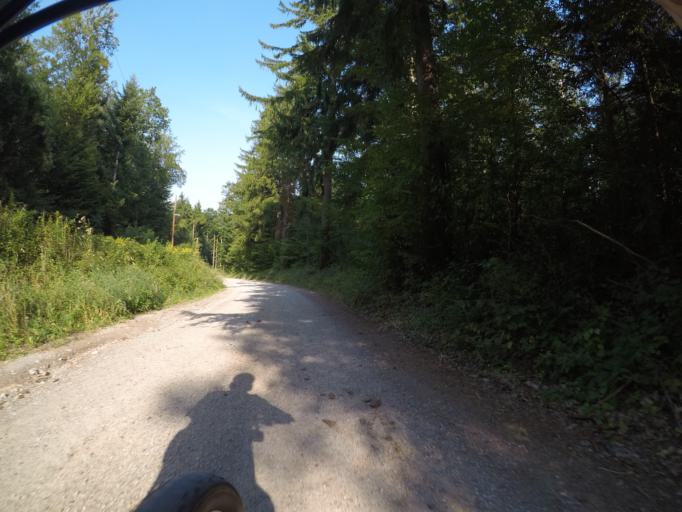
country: AT
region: Lower Austria
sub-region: Politischer Bezirk Baden
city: Berndorf
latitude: 47.9672
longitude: 16.1405
